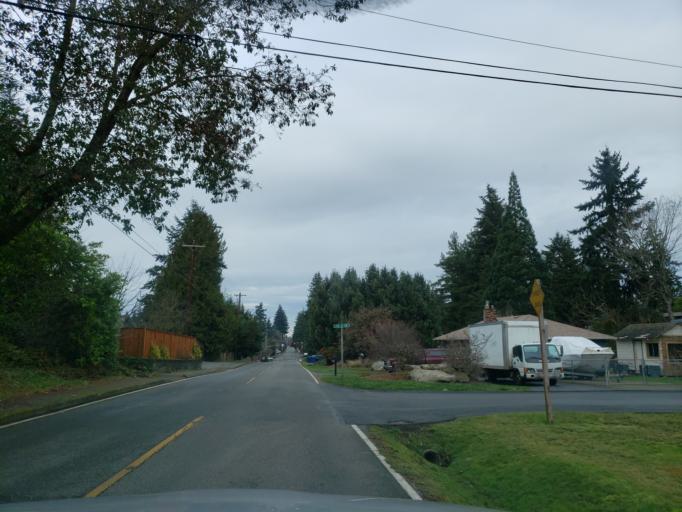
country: US
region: Washington
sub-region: Snohomish County
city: Lynnwood
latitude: 47.8194
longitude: -122.3413
